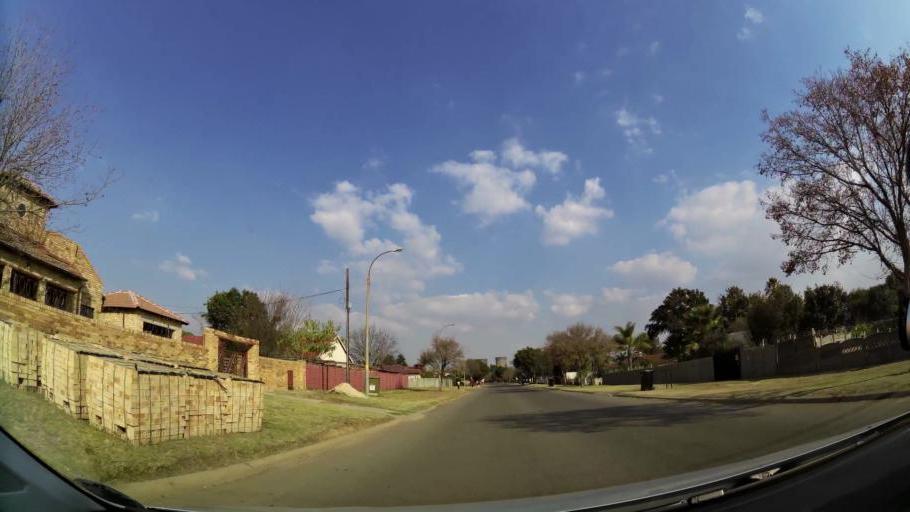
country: ZA
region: Gauteng
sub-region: City of Johannesburg Metropolitan Municipality
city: Modderfontein
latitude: -26.0998
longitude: 28.1928
